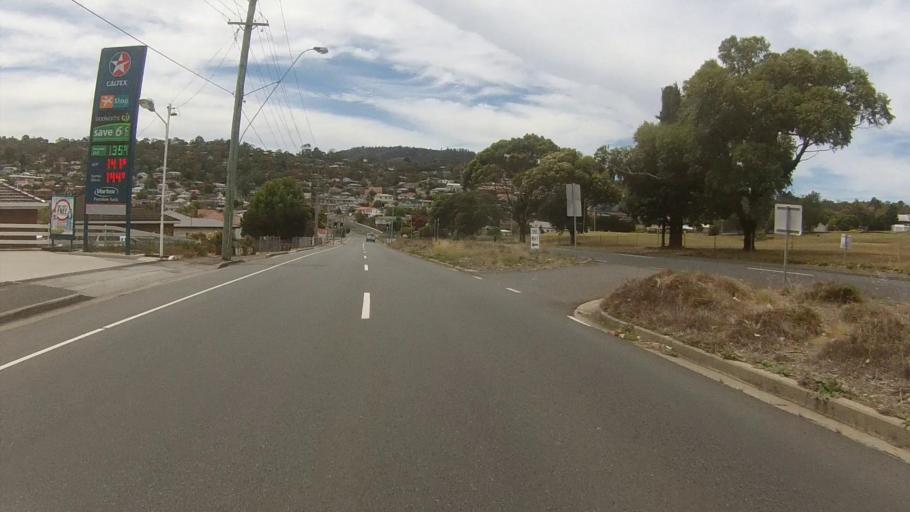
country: AU
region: Tasmania
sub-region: Clarence
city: Lindisfarne
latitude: -42.8517
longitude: 147.3606
